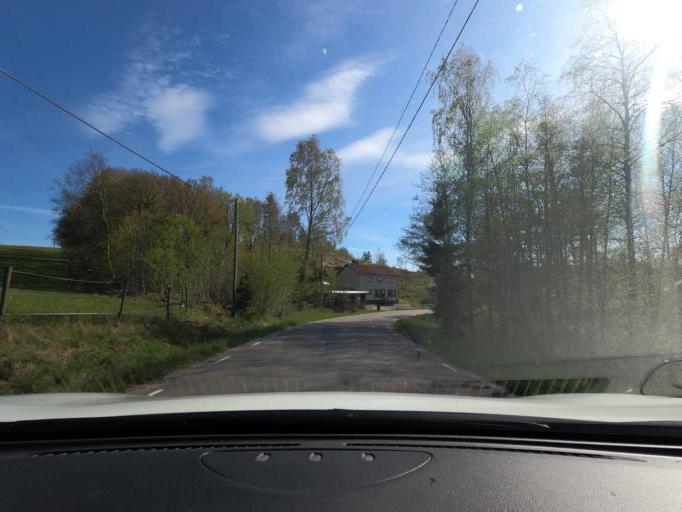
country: SE
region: Vaestra Goetaland
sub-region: Harryda Kommun
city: Hindas
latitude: 57.6456
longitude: 12.3547
